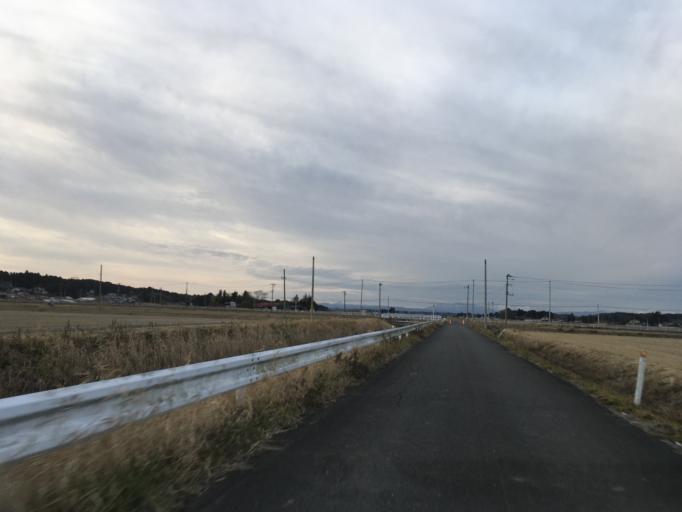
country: JP
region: Miyagi
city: Kogota
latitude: 38.6454
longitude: 141.0579
